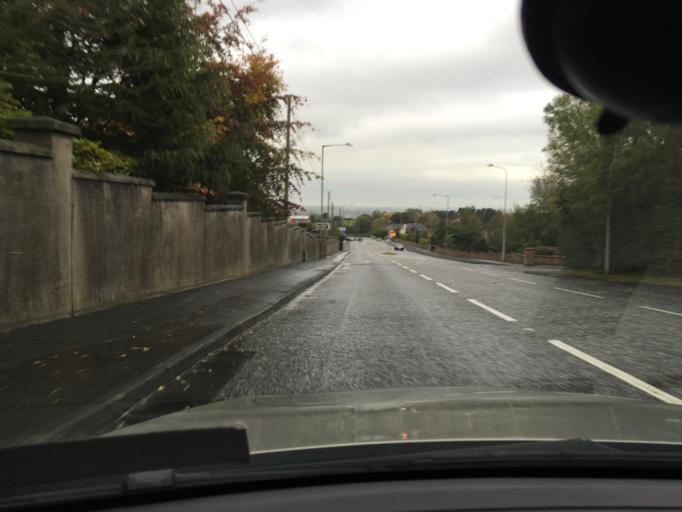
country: GB
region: Northern Ireland
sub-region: Newry and Mourne District
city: Newry
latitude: 54.1554
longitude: -6.3465
